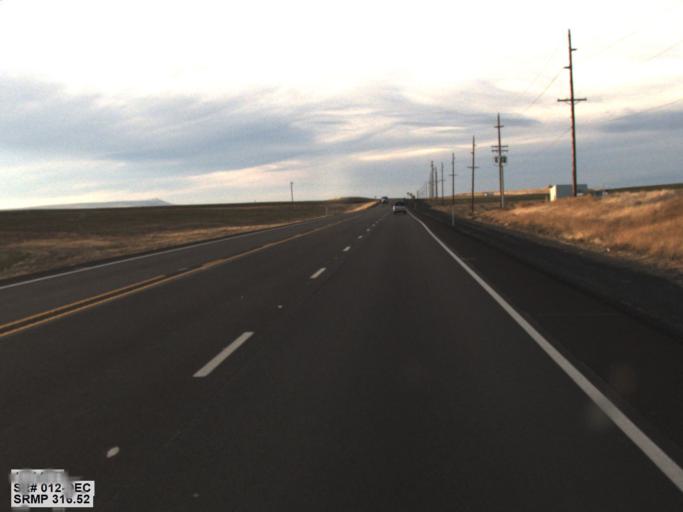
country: US
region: Washington
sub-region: Walla Walla County
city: Burbank
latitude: 46.0603
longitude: -118.7360
